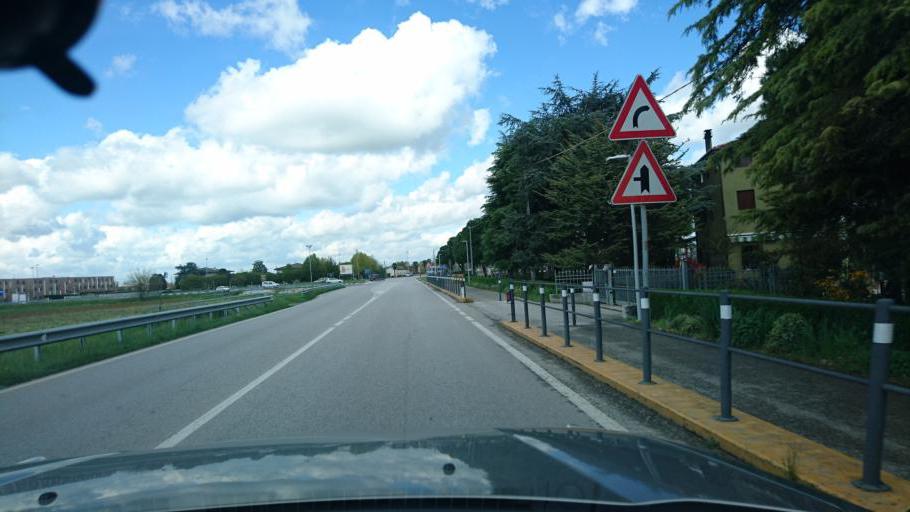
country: IT
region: Veneto
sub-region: Provincia di Padova
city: Tremignon
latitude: 45.5276
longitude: 11.7945
